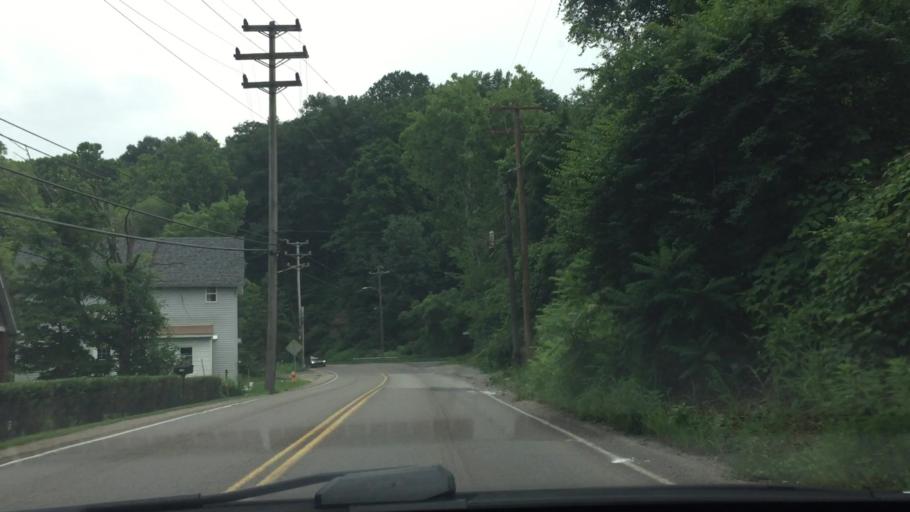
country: US
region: Pennsylvania
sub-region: Allegheny County
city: Upper Saint Clair
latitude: 40.3622
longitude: -80.0814
